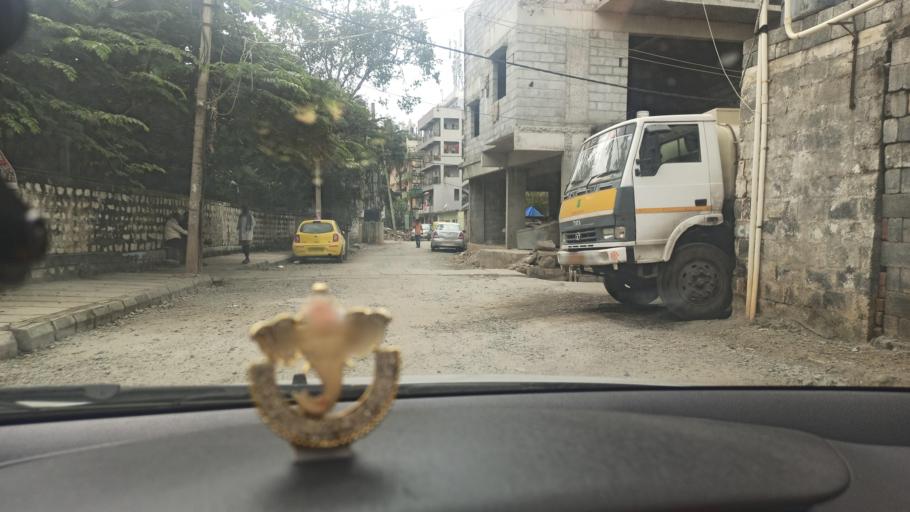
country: IN
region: Karnataka
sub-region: Bangalore Urban
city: Bangalore
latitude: 12.9201
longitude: 77.6377
